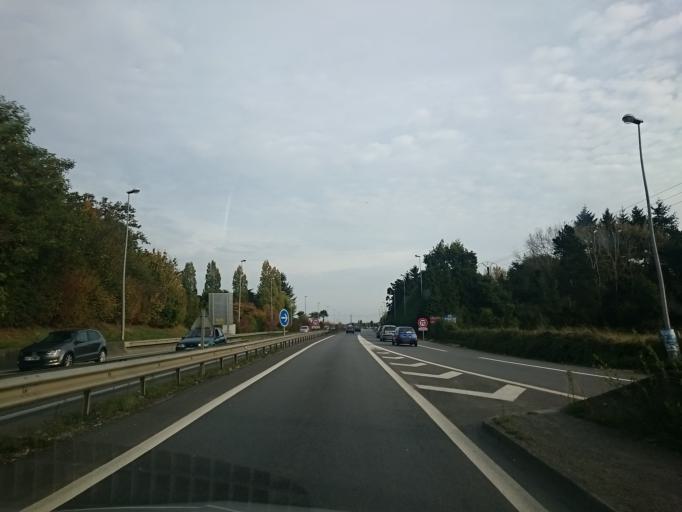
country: FR
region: Brittany
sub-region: Departement d'Ille-et-Vilaine
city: Chantepie
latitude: 48.0816
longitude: -1.6387
